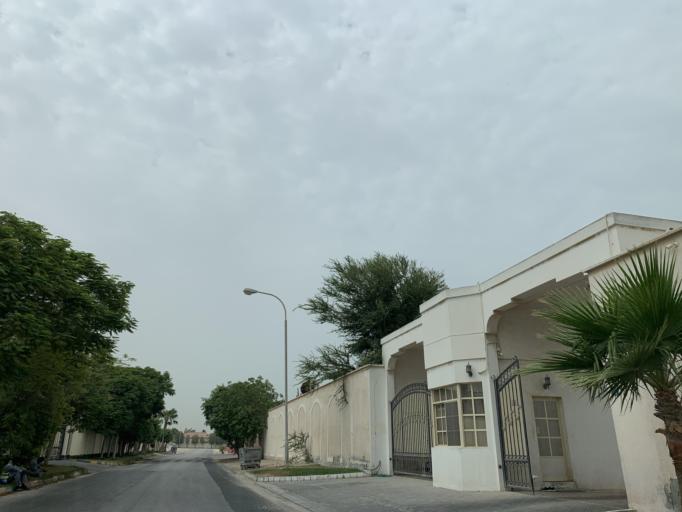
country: BH
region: Central Governorate
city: Madinat Hamad
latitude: 26.1816
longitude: 50.4712
